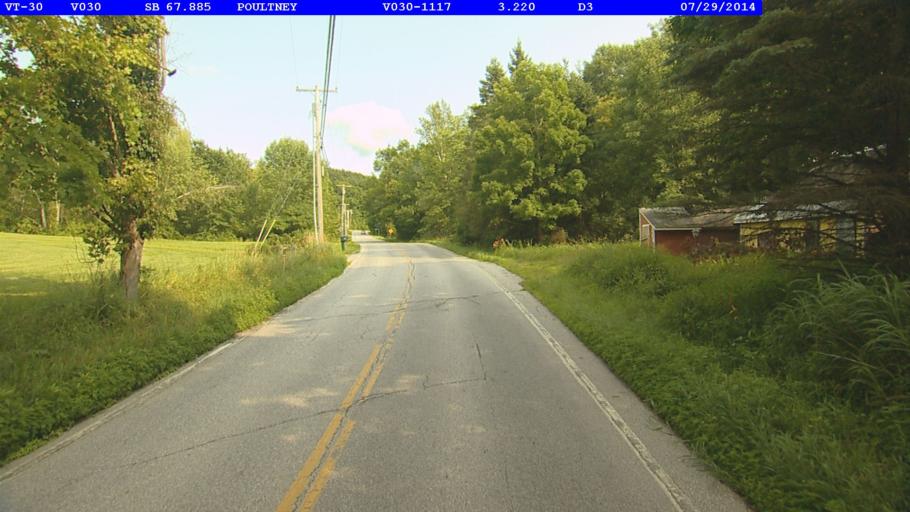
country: US
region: Vermont
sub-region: Rutland County
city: Poultney
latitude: 43.5067
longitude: -73.2134
